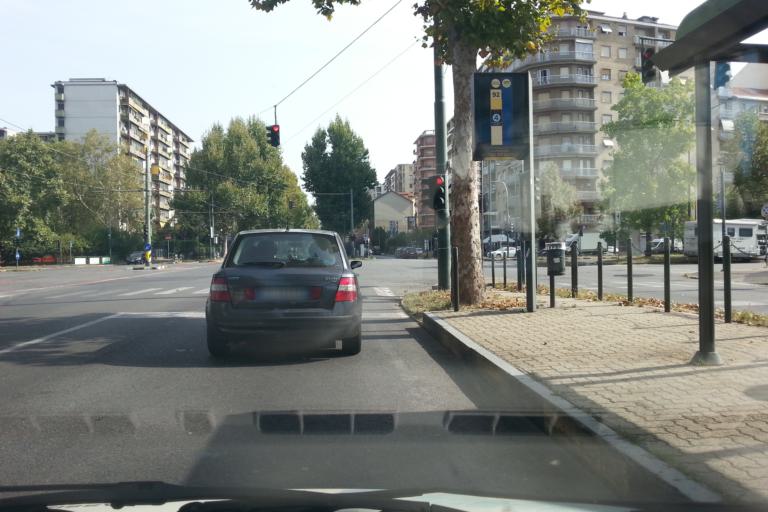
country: IT
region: Piedmont
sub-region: Provincia di Torino
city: Lesna
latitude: 45.0323
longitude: 7.6461
